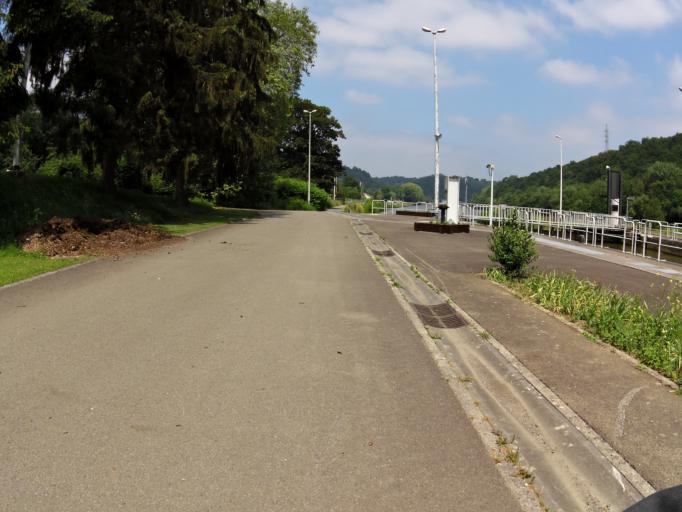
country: BE
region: Wallonia
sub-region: Province de Namur
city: Hastiere-Lavaux
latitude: 50.2042
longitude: 4.8186
